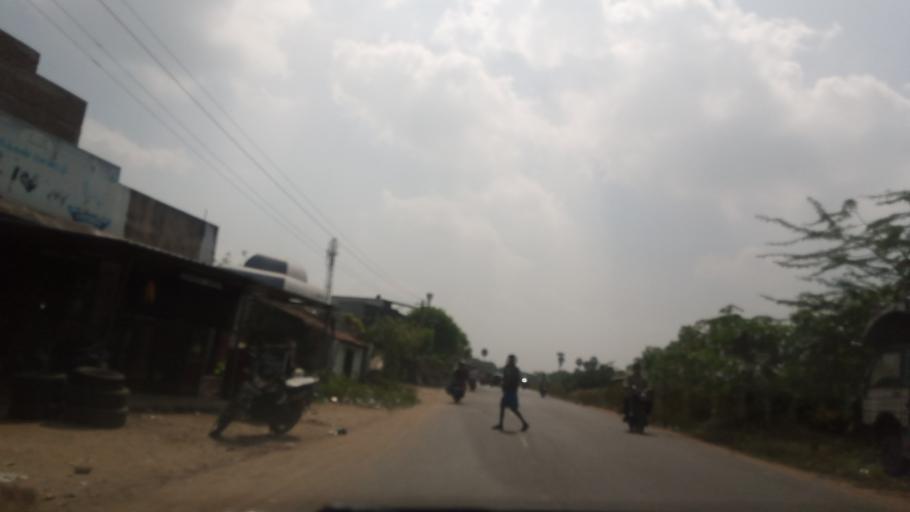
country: IN
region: Tamil Nadu
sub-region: Vellore
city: Arakkonam
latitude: 13.0735
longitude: 79.6714
